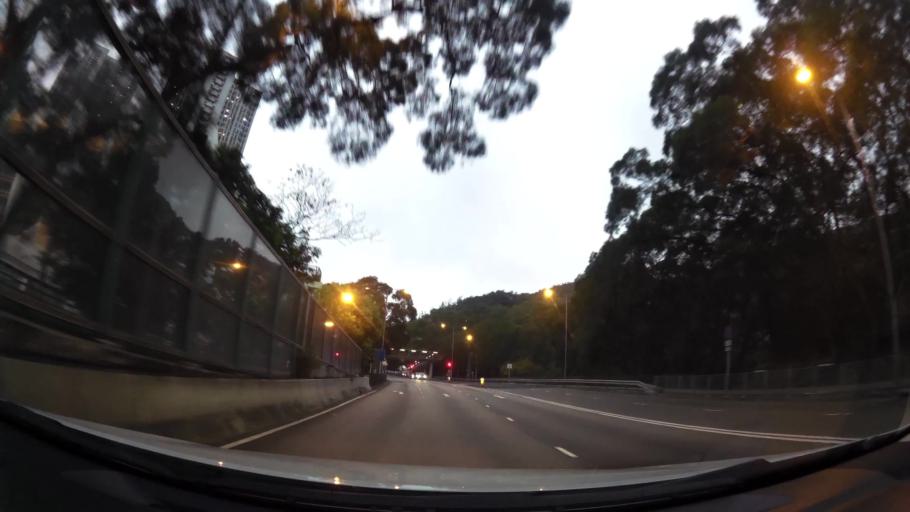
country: HK
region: Tsuen Wan
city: Tsuen Wan
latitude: 22.3504
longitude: 114.0976
